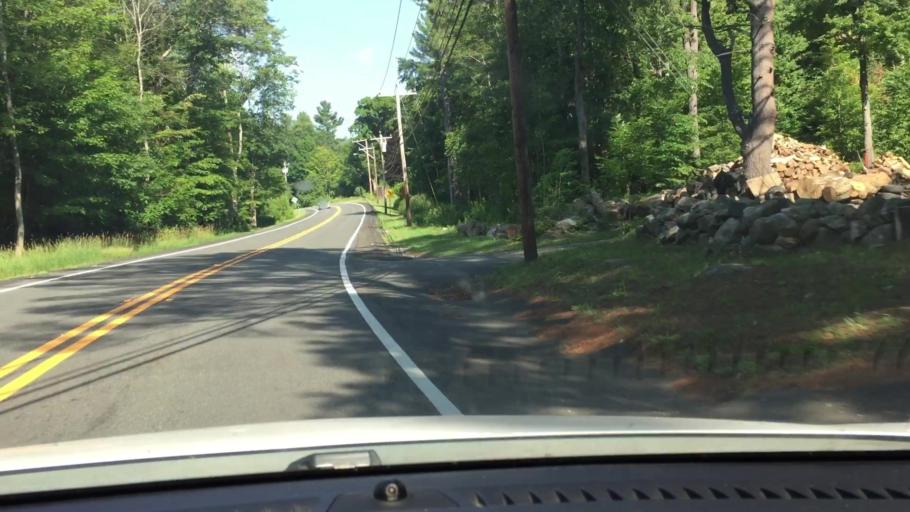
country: US
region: Massachusetts
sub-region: Berkshire County
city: Otis
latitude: 42.1929
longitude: -73.0842
